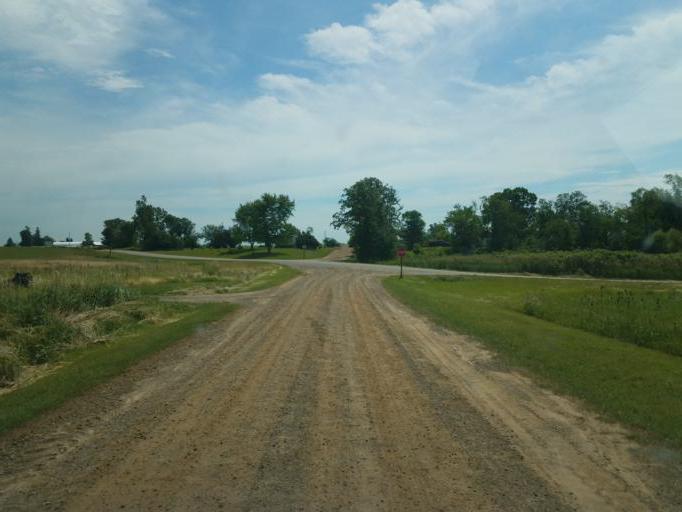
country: US
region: Michigan
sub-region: Barry County
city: Nashville
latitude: 42.6551
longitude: -84.9691
